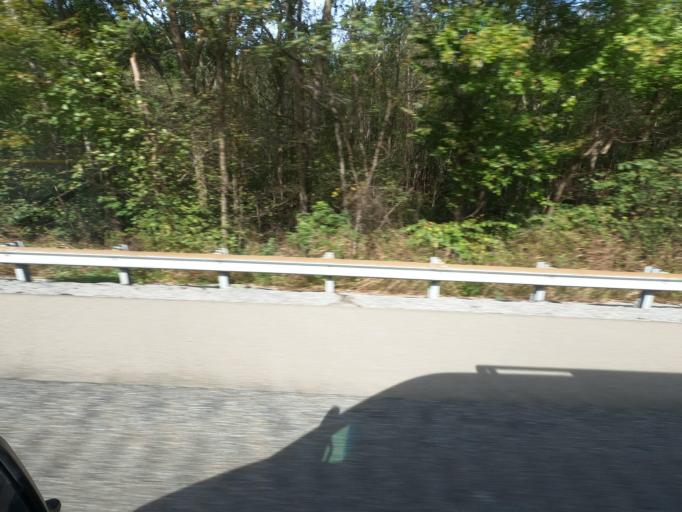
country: US
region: Tennessee
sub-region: Humphreys County
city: New Johnsonville
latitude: 35.8723
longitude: -87.8615
